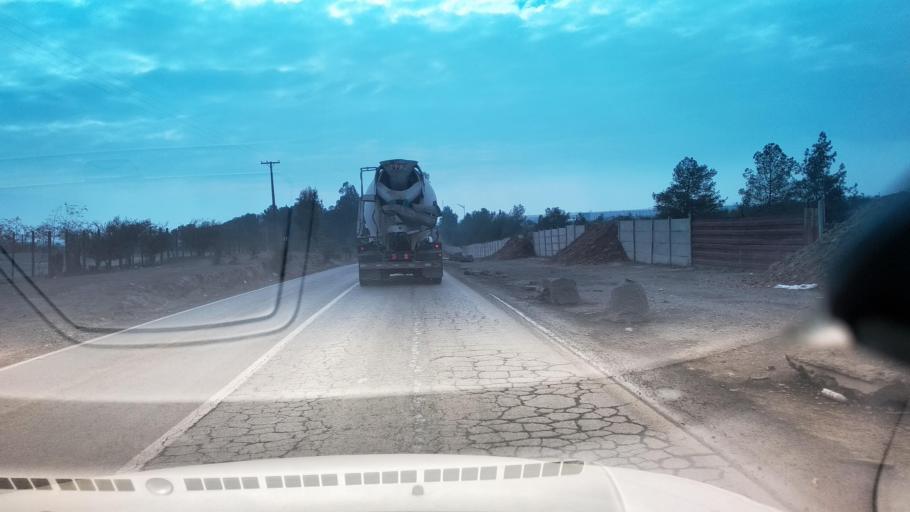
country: CL
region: Santiago Metropolitan
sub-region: Provincia de Santiago
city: Lo Prado
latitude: -33.4506
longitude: -70.7990
